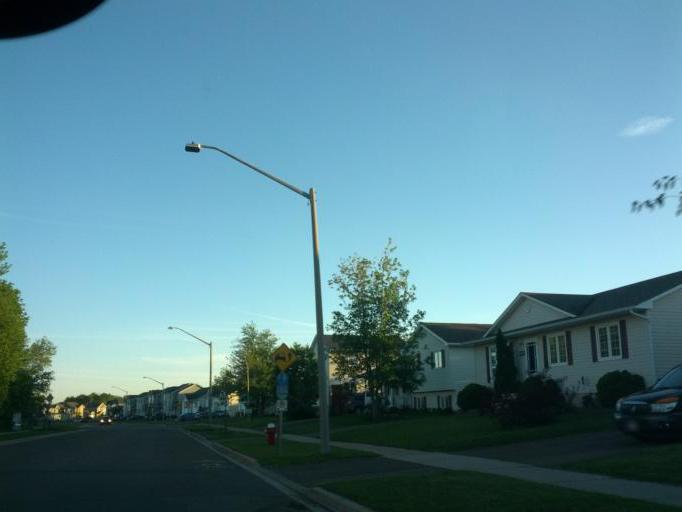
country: CA
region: New Brunswick
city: Moncton
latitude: 46.1147
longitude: -64.8615
